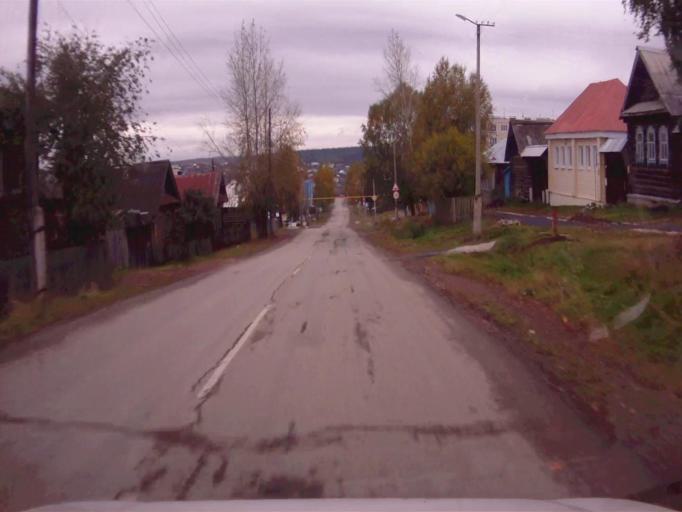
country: RU
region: Chelyabinsk
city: Nyazepetrovsk
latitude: 56.0574
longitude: 59.6079
